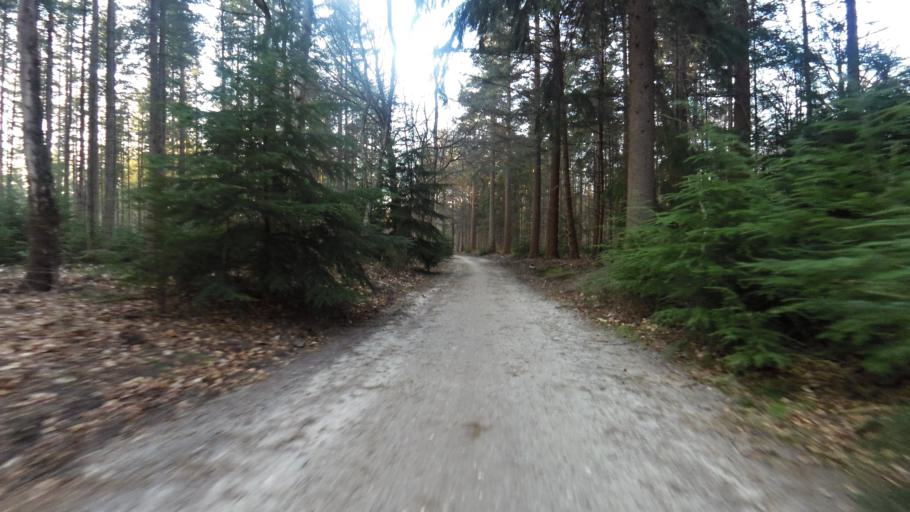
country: NL
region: Gelderland
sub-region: Gemeente Barneveld
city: Garderen
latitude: 52.2491
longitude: 5.6774
